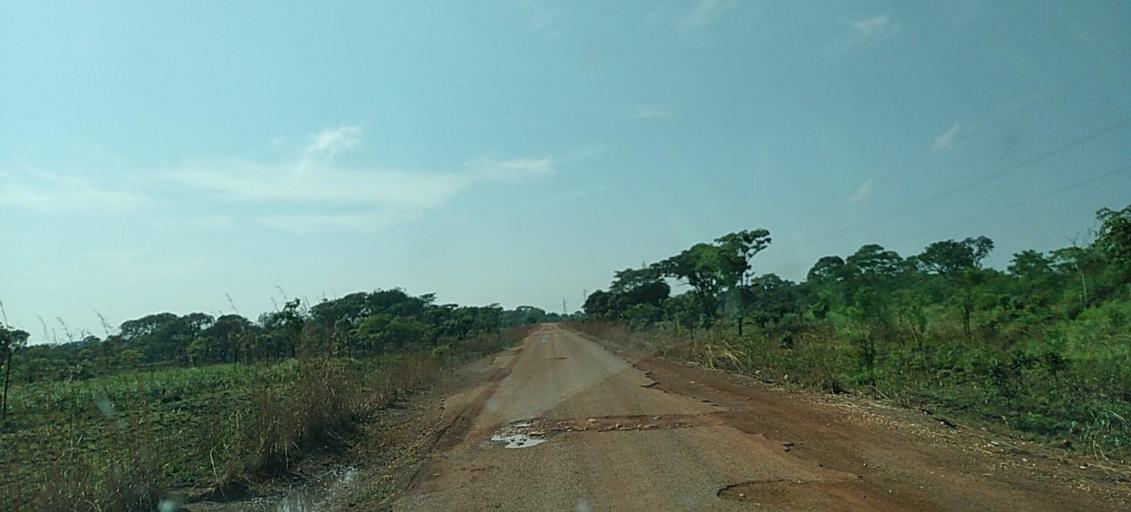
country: ZM
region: North-Western
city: Mwinilunga
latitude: -11.8173
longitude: 25.0922
